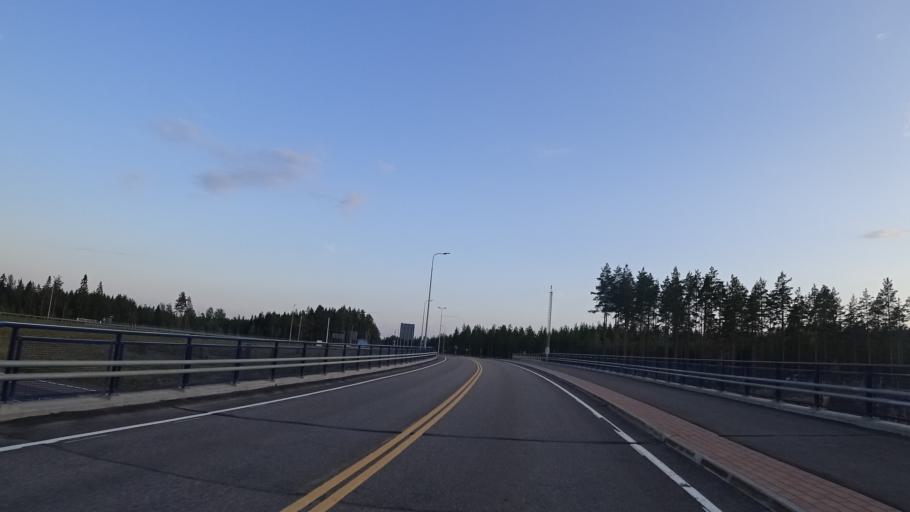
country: FI
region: Kymenlaakso
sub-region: Kotka-Hamina
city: Virojoki
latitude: 60.6058
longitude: 27.7043
